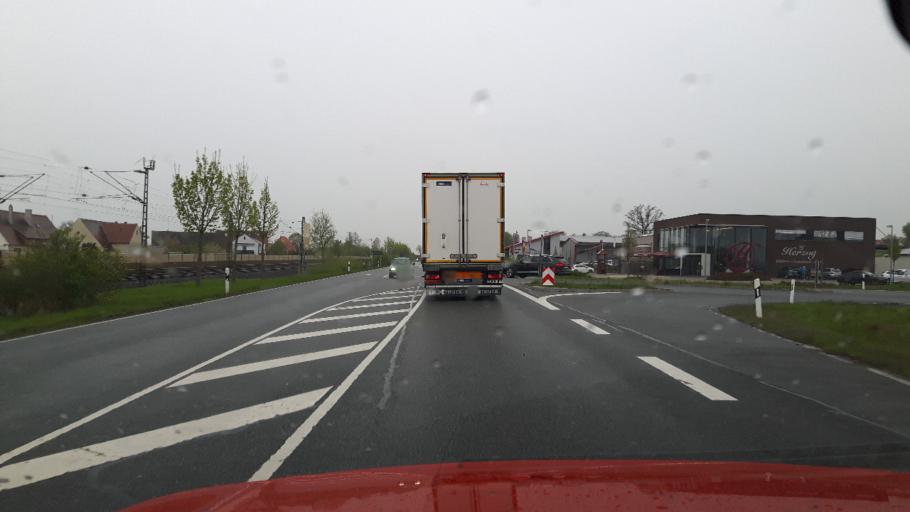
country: DE
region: Bavaria
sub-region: Regierungsbezirk Mittelfranken
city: Muhr am See
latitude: 49.1523
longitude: 10.7261
